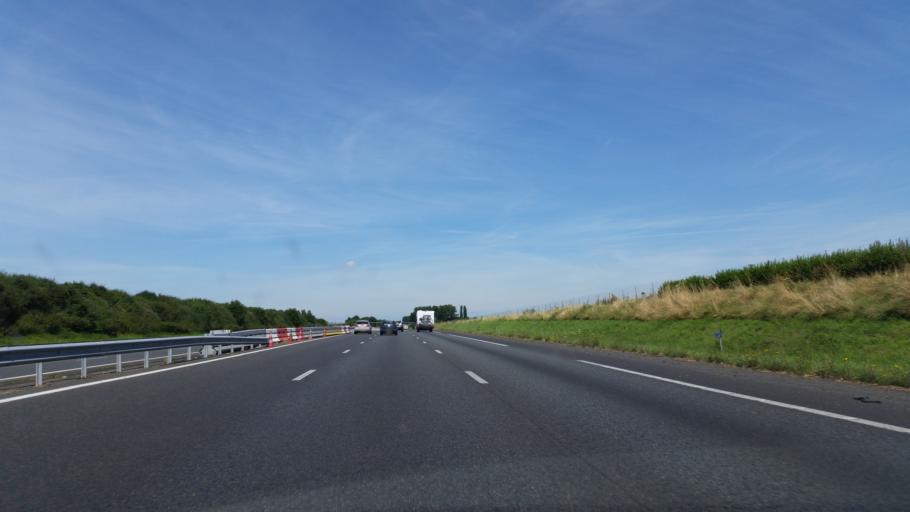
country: FR
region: Nord-Pas-de-Calais
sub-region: Departement du Pas-de-Calais
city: Vaulx-Vraucourt
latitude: 50.1407
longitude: 2.8724
